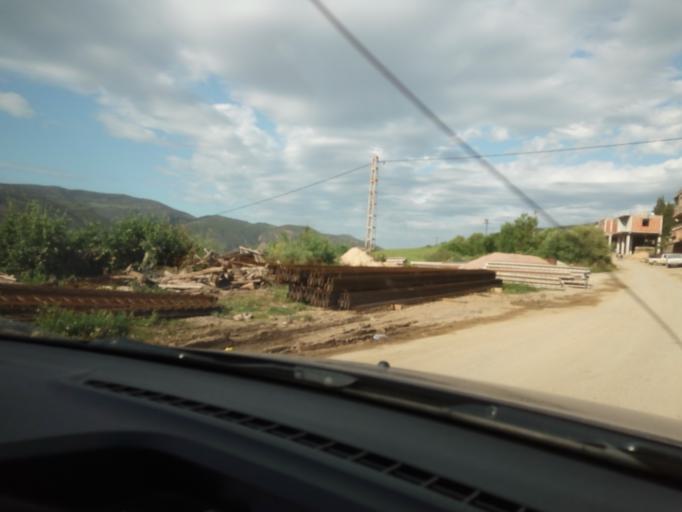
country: DZ
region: Tipaza
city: Hadjout
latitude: 36.3732
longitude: 2.4923
